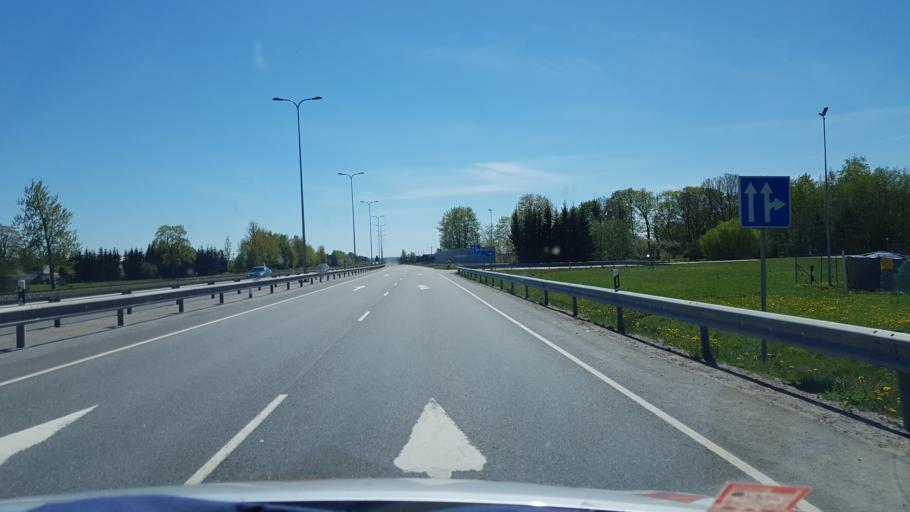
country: EE
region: Tartu
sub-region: UElenurme vald
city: Ulenurme
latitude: 58.3353
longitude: 26.7135
